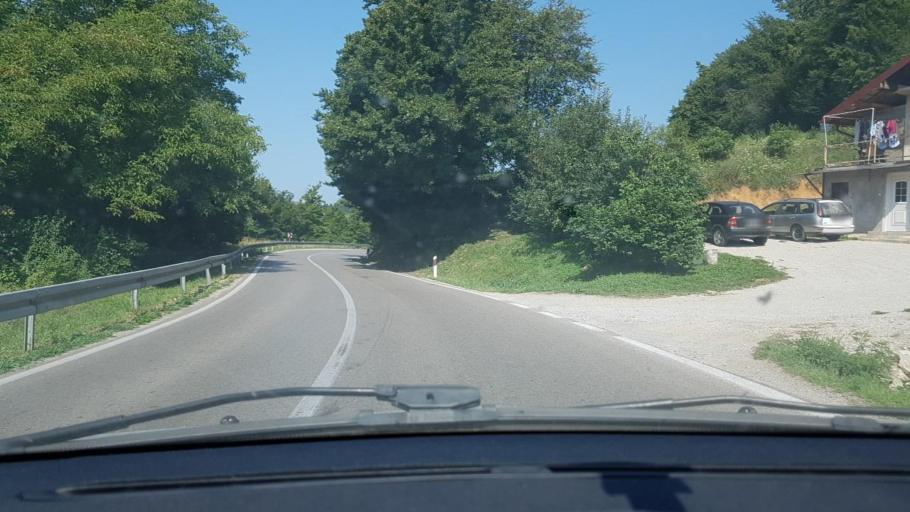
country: BA
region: Federation of Bosnia and Herzegovina
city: Mala Kladusa
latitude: 45.1516
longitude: 15.8363
